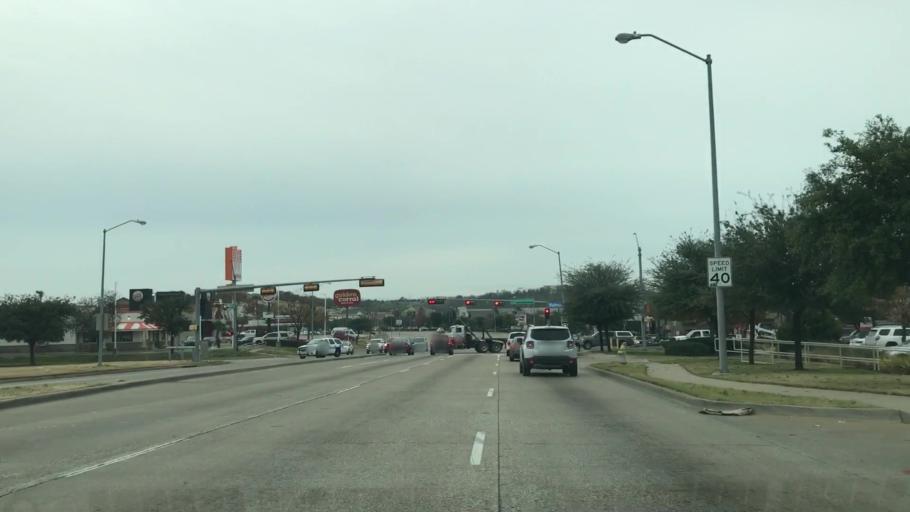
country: US
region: Texas
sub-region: Dallas County
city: Cockrell Hill
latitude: 32.7655
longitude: -96.8959
